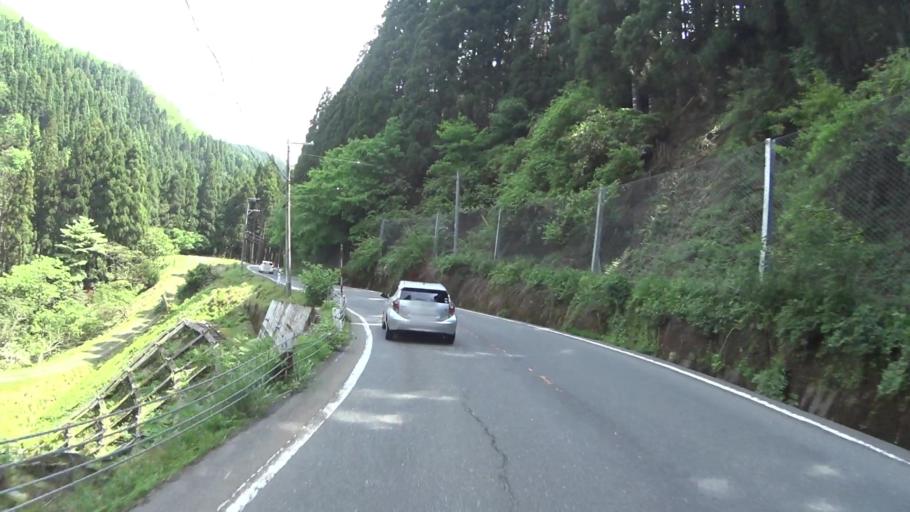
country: JP
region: Shiga Prefecture
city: Kitahama
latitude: 35.3772
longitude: 135.9226
